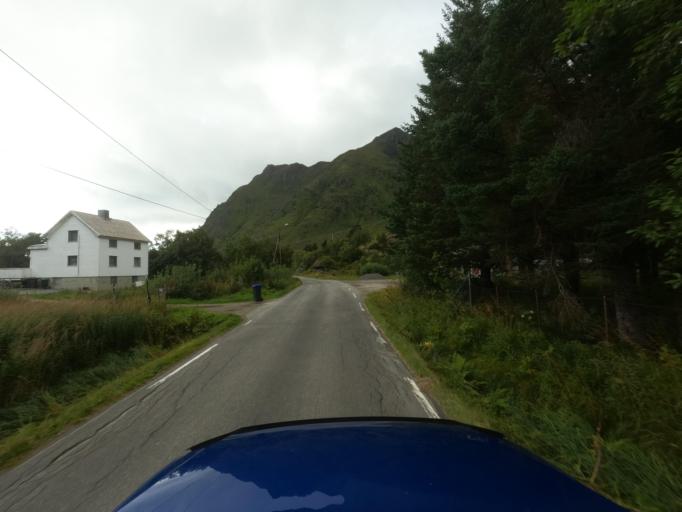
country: NO
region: Nordland
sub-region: Vestvagoy
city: Evjen
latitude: 68.1948
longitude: 13.9397
